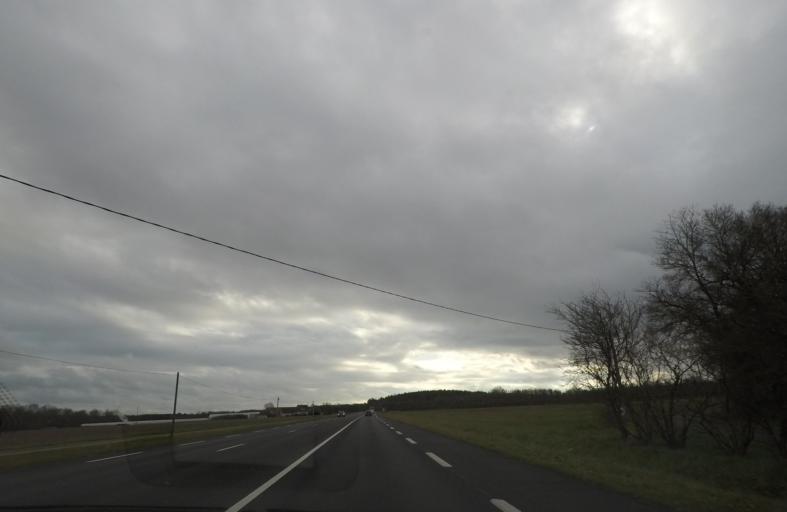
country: FR
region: Centre
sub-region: Departement du Loir-et-Cher
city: Soings-en-Sologne
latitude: 47.4436
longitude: 1.5433
